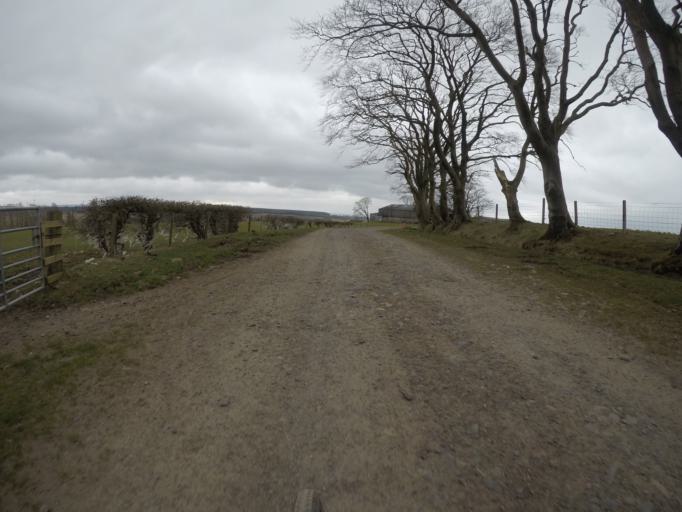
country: GB
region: Scotland
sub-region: East Ayrshire
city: Galston
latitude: 55.6675
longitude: -4.3746
